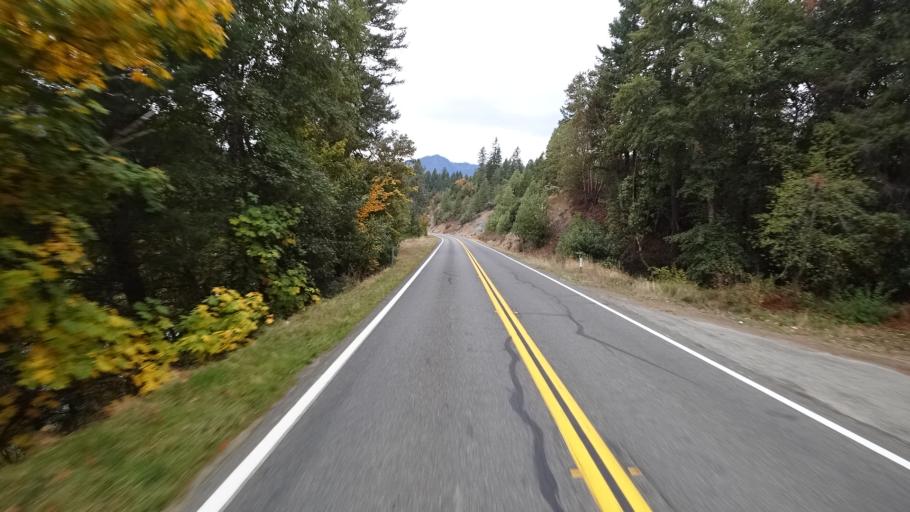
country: US
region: California
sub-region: Siskiyou County
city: Happy Camp
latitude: 41.7859
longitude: -123.3935
